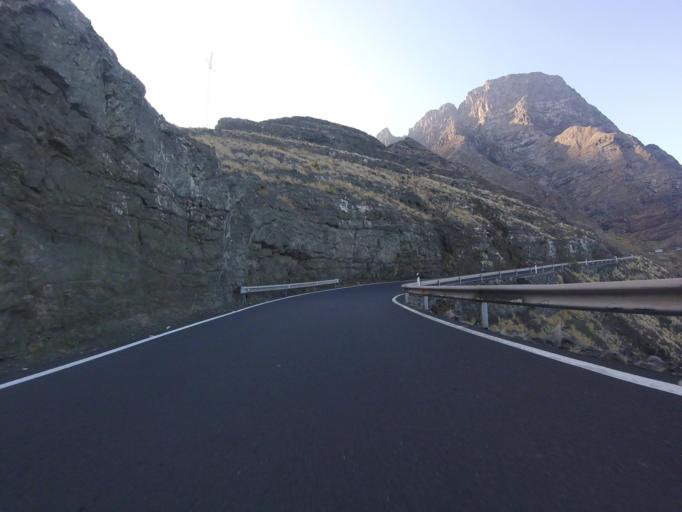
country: ES
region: Canary Islands
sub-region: Provincia de Las Palmas
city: Agaete
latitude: 28.0744
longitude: -15.7156
